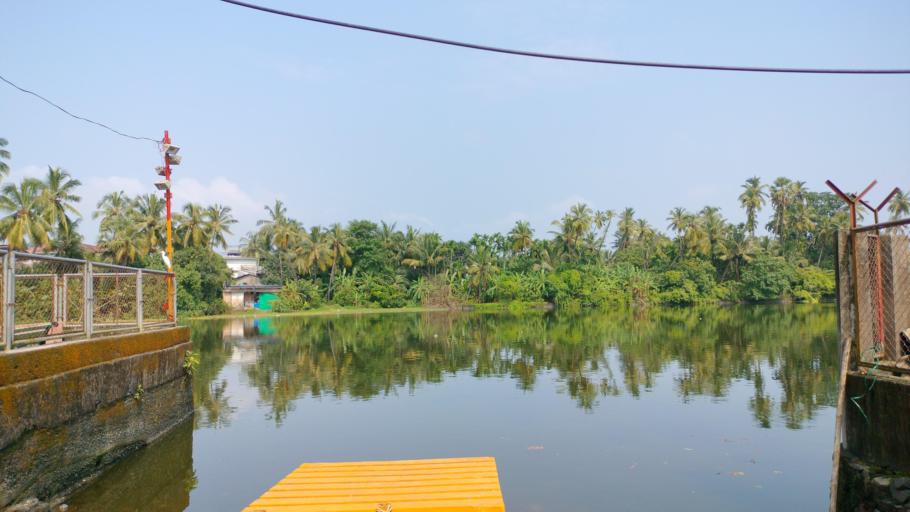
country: IN
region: Maharashtra
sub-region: Thane
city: Virar
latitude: 19.4262
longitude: 72.7823
